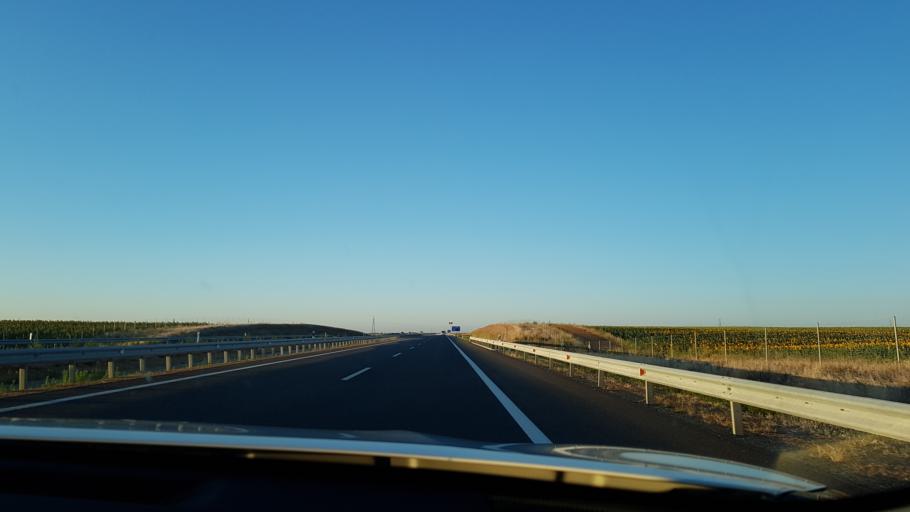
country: ES
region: Castille and Leon
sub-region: Provincia de Zamora
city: Roales
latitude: 41.5936
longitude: -5.7806
